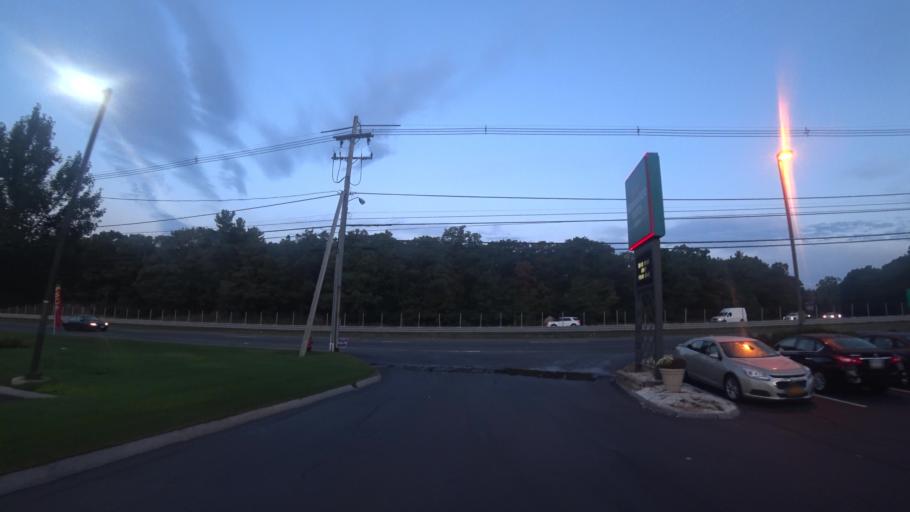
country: US
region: Massachusetts
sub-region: Essex County
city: South Peabody
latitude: 42.5255
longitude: -70.9949
